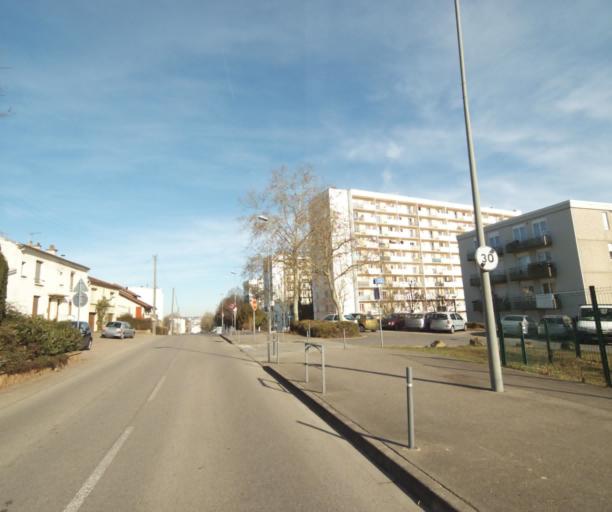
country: FR
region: Lorraine
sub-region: Departement de Meurthe-et-Moselle
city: Vandoeuvre-les-Nancy
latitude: 48.6594
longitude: 6.1701
